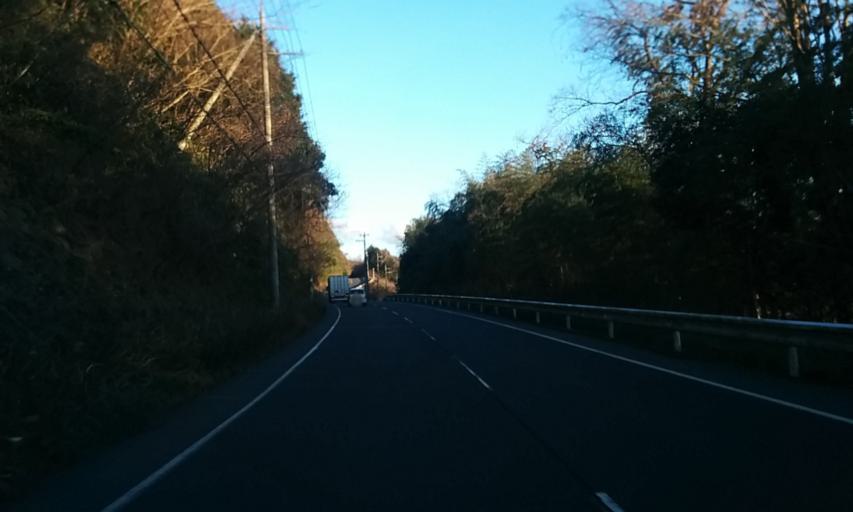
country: JP
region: Kyoto
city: Ayabe
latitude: 35.3098
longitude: 135.2643
